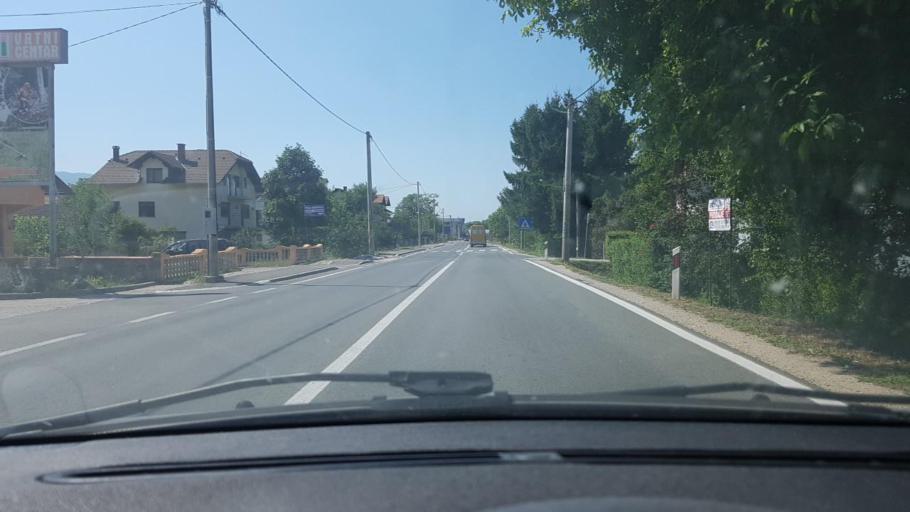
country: BA
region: Federation of Bosnia and Herzegovina
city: Bihac
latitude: 44.7938
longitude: 15.9238
